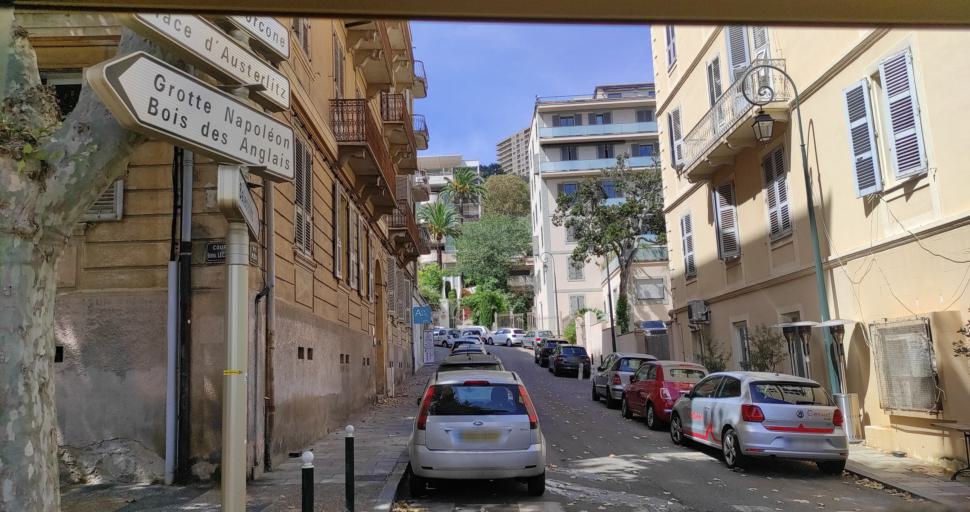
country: FR
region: Corsica
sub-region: Departement de la Corse-du-Sud
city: Ajaccio
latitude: 41.9177
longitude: 8.7311
